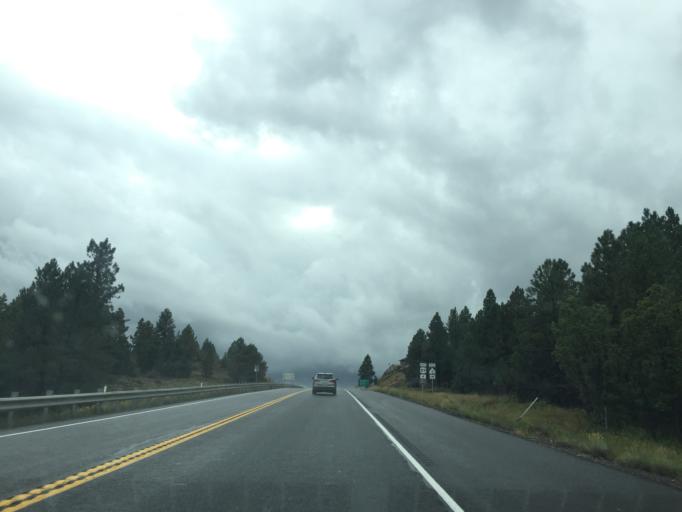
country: US
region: Utah
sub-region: Garfield County
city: Panguitch
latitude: 37.4918
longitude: -112.5107
